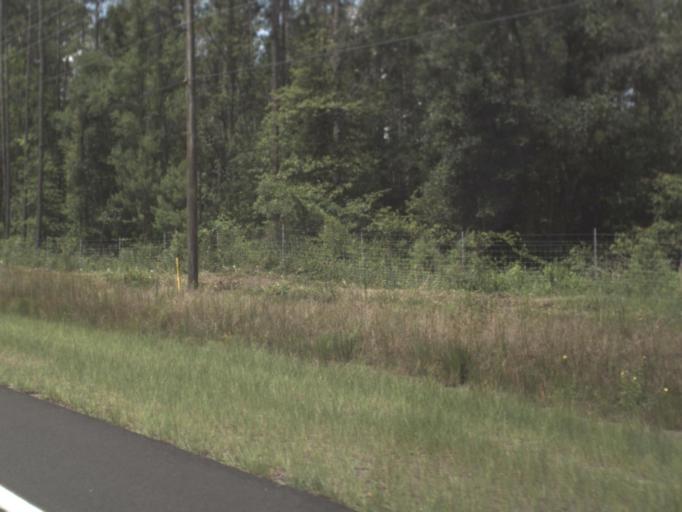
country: US
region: Florida
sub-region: Duval County
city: Baldwin
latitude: 30.4174
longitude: -81.9286
